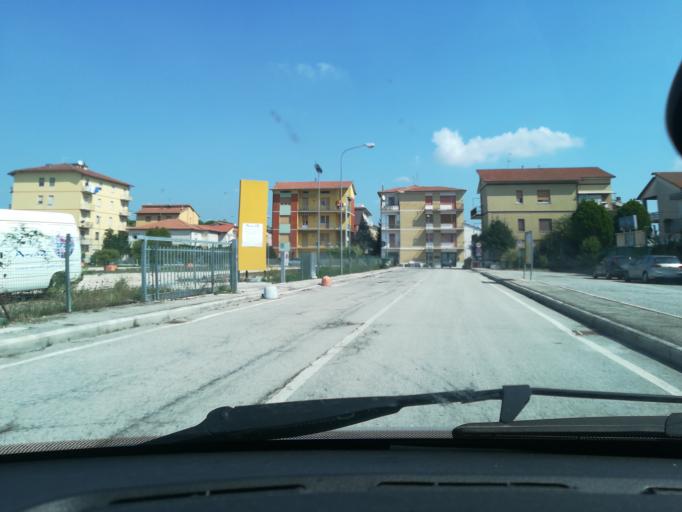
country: IT
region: The Marches
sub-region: Provincia di Macerata
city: Casette Verdini
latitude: 43.2507
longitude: 13.4076
